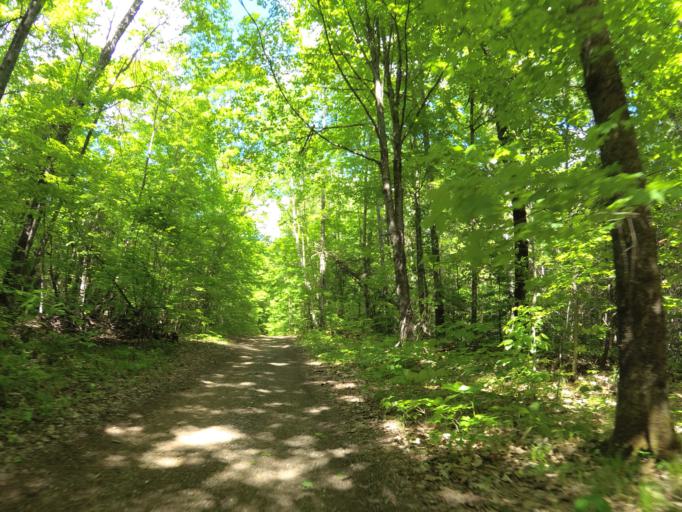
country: CA
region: Ontario
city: Renfrew
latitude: 45.0473
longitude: -76.8297
